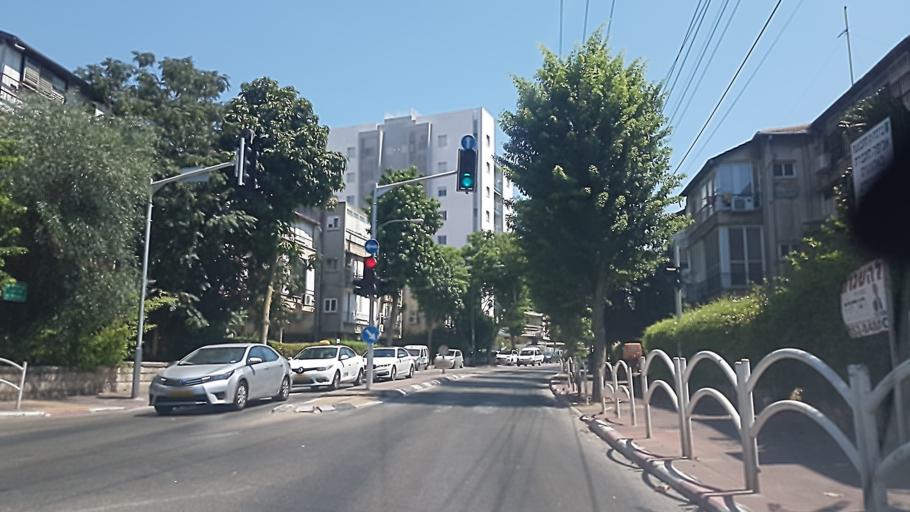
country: IL
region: Tel Aviv
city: Bene Beraq
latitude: 32.0826
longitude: 34.8254
